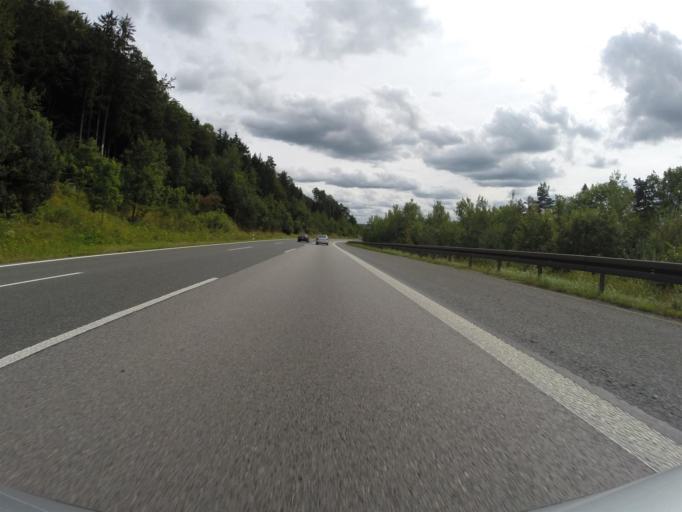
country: DE
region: Bavaria
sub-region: Regierungsbezirk Mittelfranken
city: Simmelsdorf
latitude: 49.5880
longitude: 11.3462
